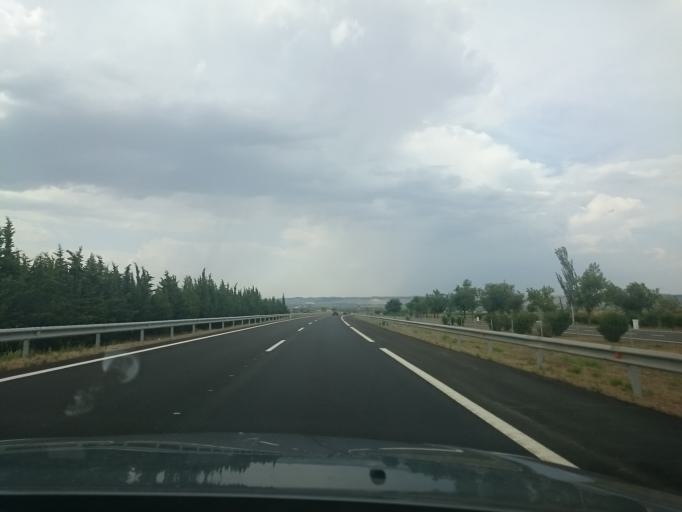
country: ES
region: La Rioja
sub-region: Provincia de La Rioja
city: Aldeanueva de Ebro
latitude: 42.2368
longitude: -1.9012
